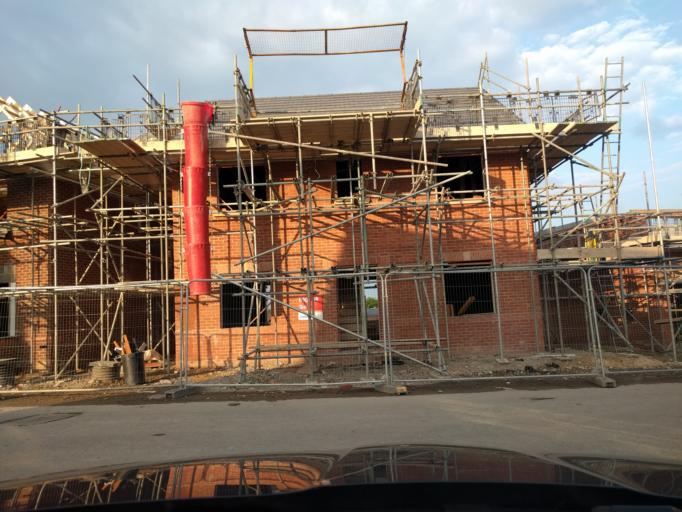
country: GB
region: England
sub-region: Northumberland
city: Choppington
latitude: 55.1348
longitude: -1.6173
